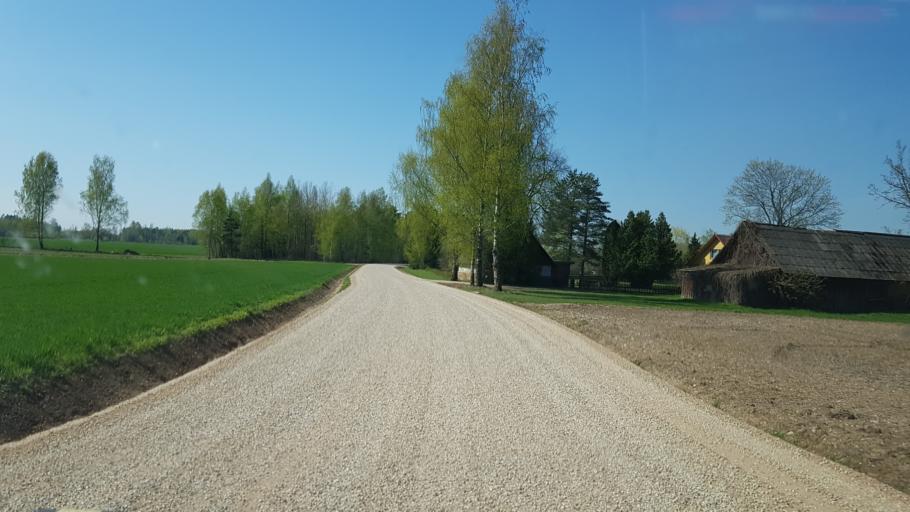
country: EE
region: Polvamaa
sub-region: Polva linn
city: Polva
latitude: 58.1300
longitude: 27.2610
